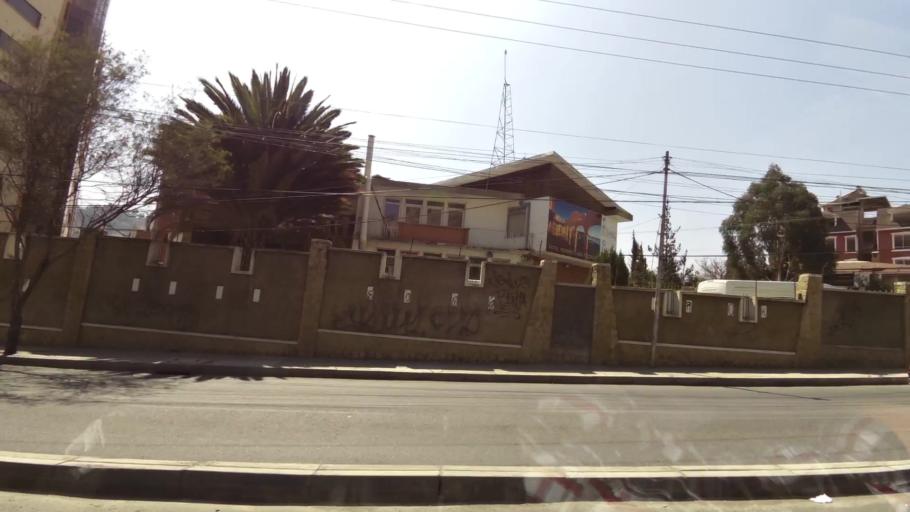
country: BO
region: La Paz
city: La Paz
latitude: -16.5452
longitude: -68.0863
